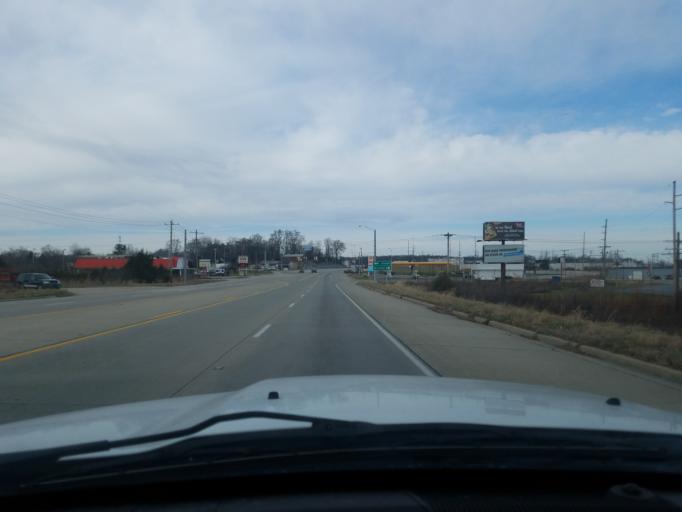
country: US
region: Indiana
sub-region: Lawrence County
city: Mitchell
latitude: 38.7301
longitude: -86.4877
